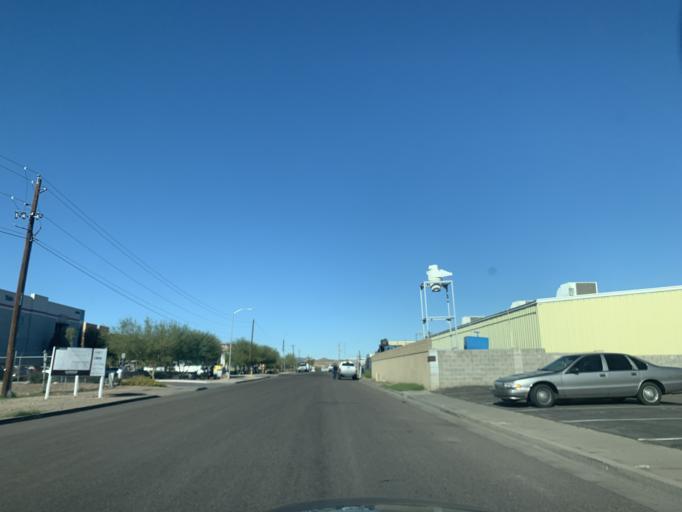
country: US
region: Arizona
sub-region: Maricopa County
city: Tempe Junction
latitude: 33.4188
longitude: -111.9869
